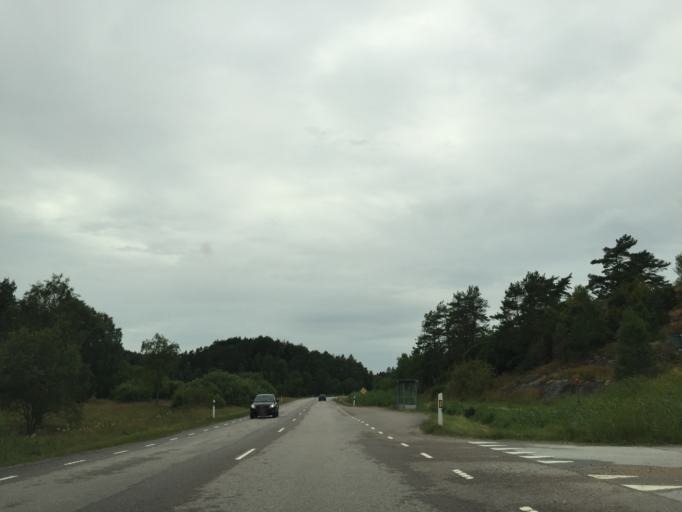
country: SE
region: Vaestra Goetaland
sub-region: Tjorns Kommun
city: Myggenas
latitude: 58.0238
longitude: 11.6829
